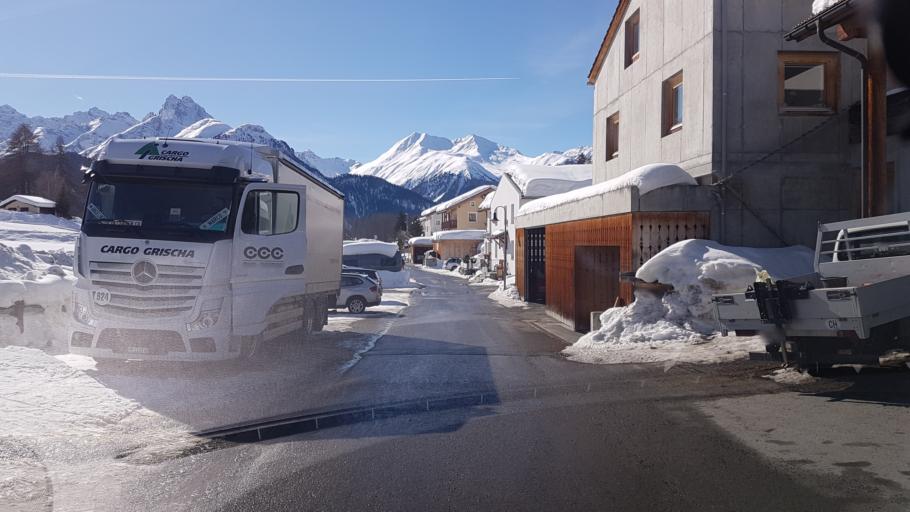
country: CH
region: Grisons
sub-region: Inn District
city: Scuol
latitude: 46.7923
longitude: 10.2449
